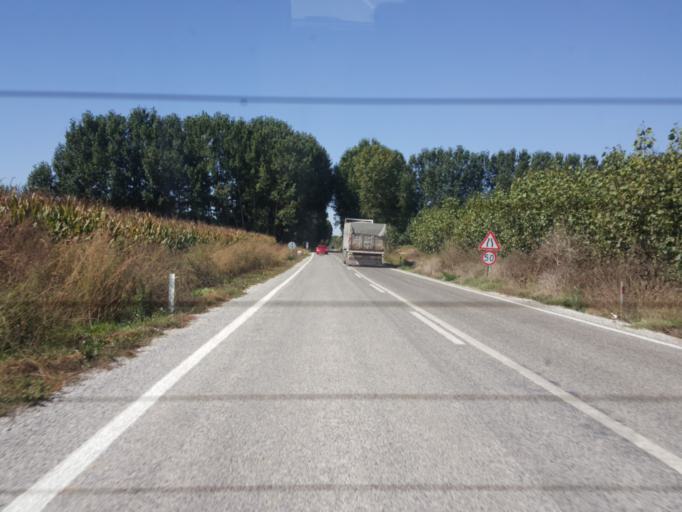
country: TR
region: Tokat
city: Pazar
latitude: 40.2679
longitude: 36.1964
